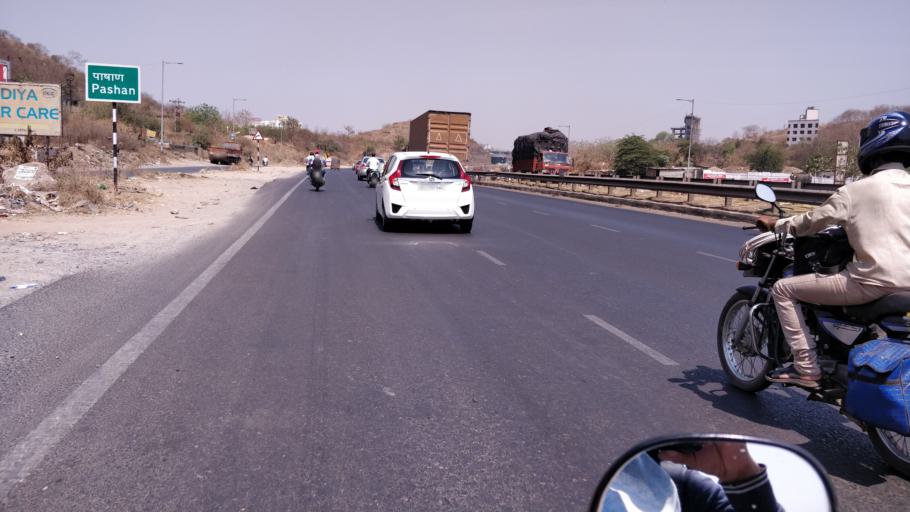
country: IN
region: Maharashtra
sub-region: Pune Division
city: Shivaji Nagar
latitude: 18.5434
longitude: 73.7758
